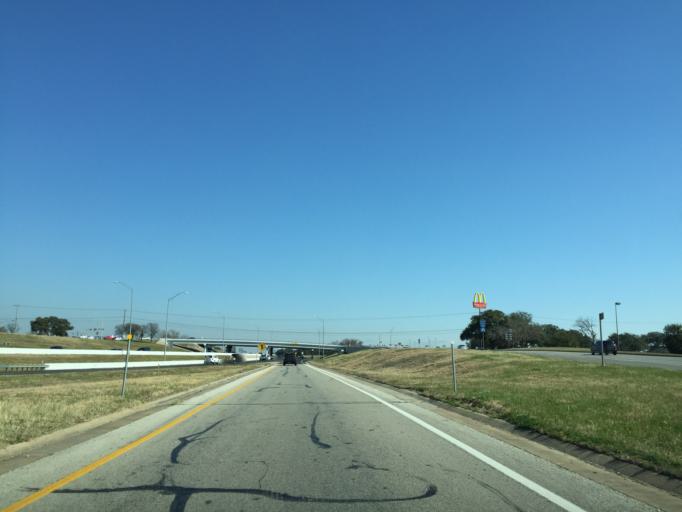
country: US
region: Texas
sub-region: Williamson County
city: Georgetown
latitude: 30.6473
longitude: -97.6812
